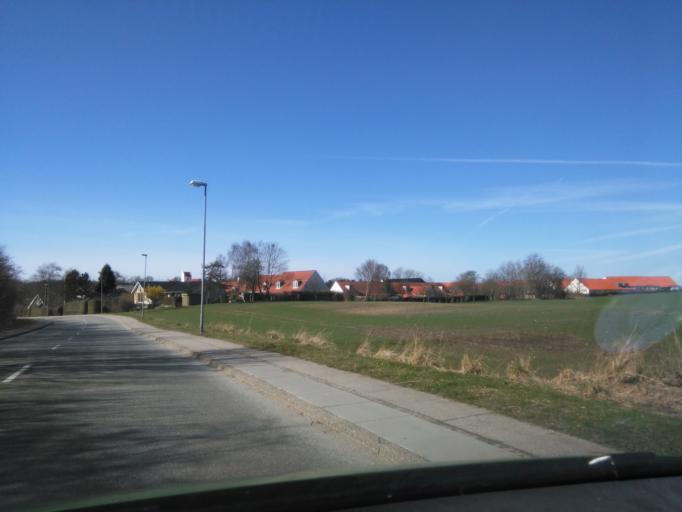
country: DK
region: Central Jutland
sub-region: Arhus Kommune
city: Lystrup
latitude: 56.2443
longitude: 10.2337
